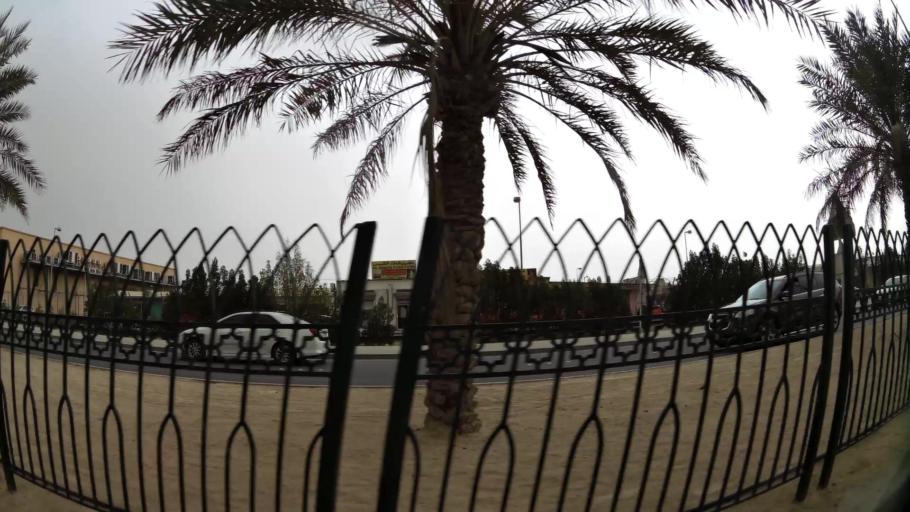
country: BH
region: Northern
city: Madinat `Isa
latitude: 26.1689
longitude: 50.5534
